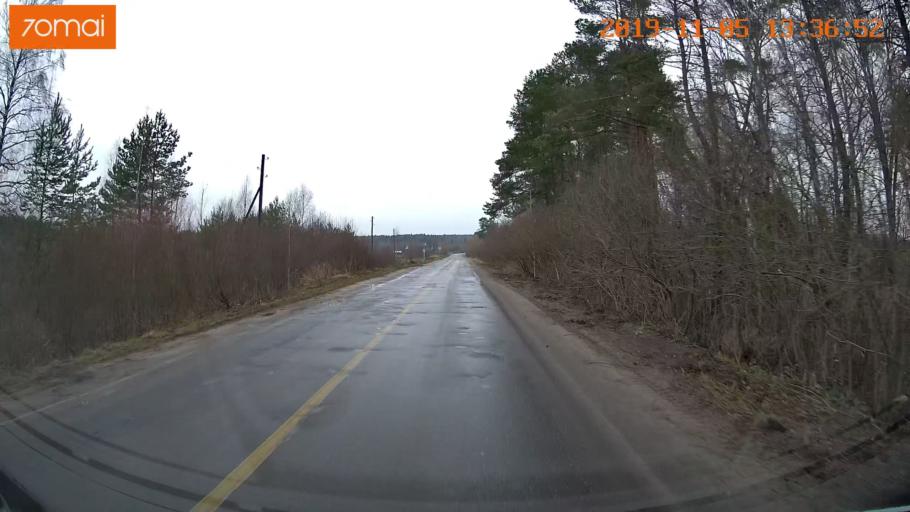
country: RU
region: Ivanovo
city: Shuya
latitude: 56.9177
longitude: 41.3821
